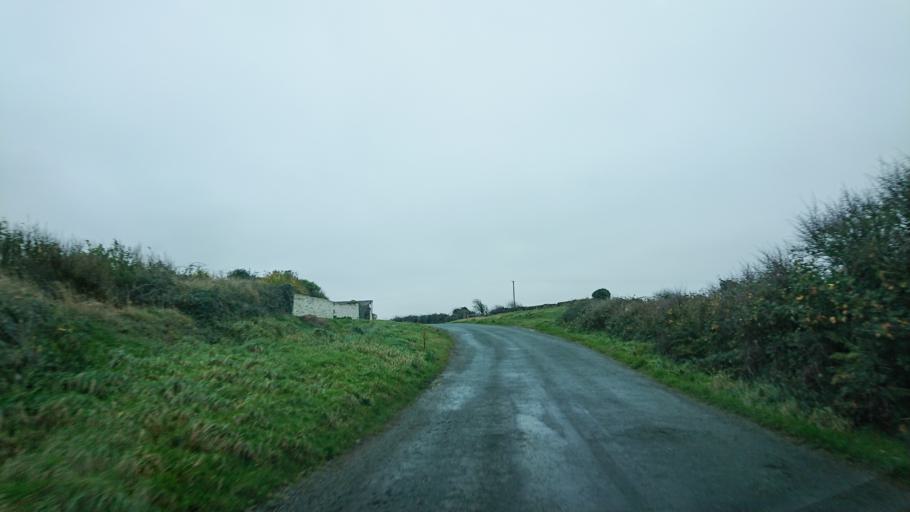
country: IE
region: Munster
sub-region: Waterford
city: Dunmore East
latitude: 52.1563
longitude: -7.0611
